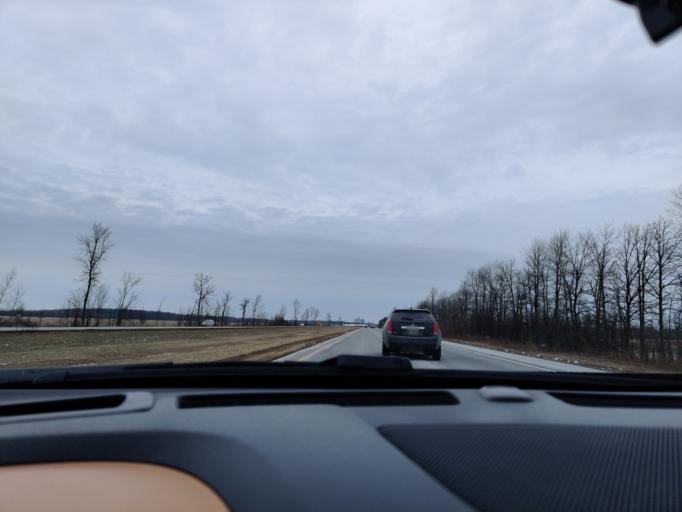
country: US
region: New York
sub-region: St. Lawrence County
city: Norfolk
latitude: 44.9014
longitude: -75.2356
